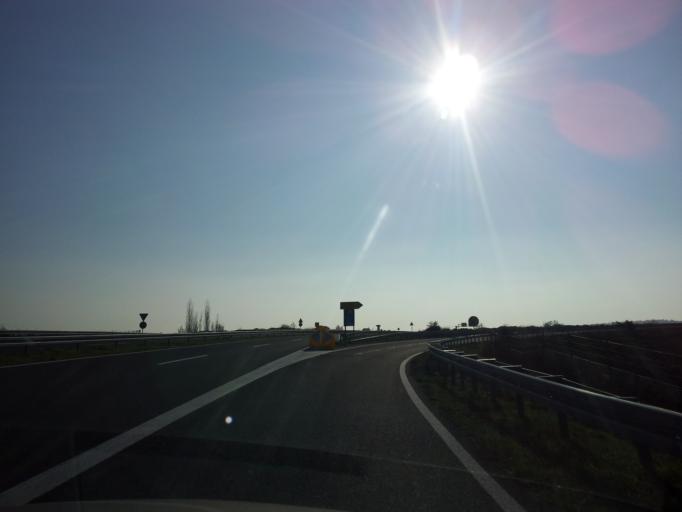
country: HR
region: Zadarska
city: Sukosan
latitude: 44.0723
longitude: 15.3425
